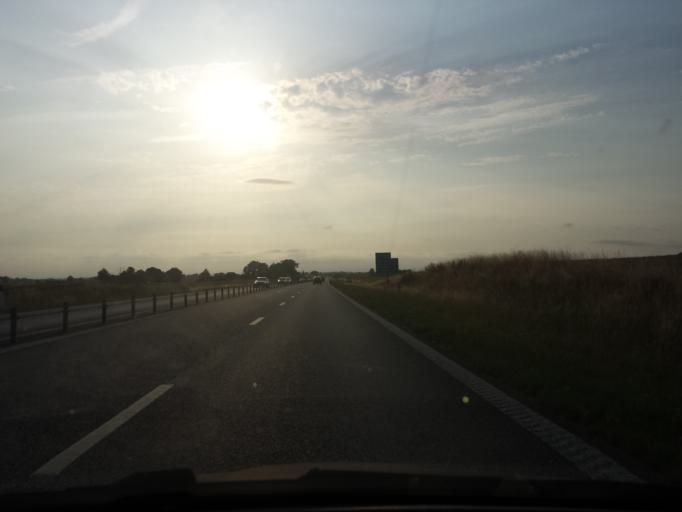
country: SE
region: Skane
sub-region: Skurups Kommun
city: Rydsgard
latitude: 55.4775
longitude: 13.6375
